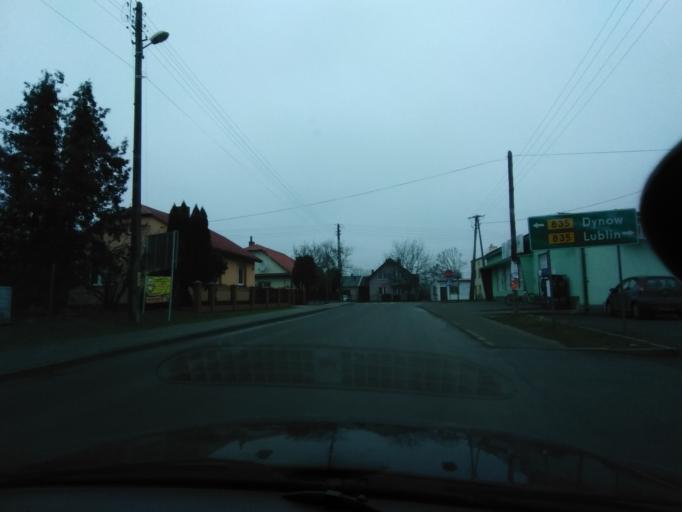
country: PL
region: Subcarpathian Voivodeship
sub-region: Powiat przeworski
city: Urzejowice
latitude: 50.0101
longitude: 22.4617
